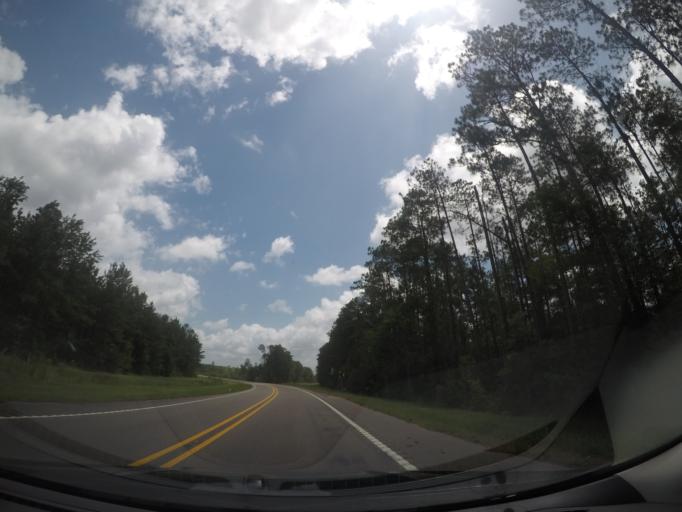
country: US
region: Mississippi
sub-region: Hancock County
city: Pearlington
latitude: 30.2981
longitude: -89.5093
